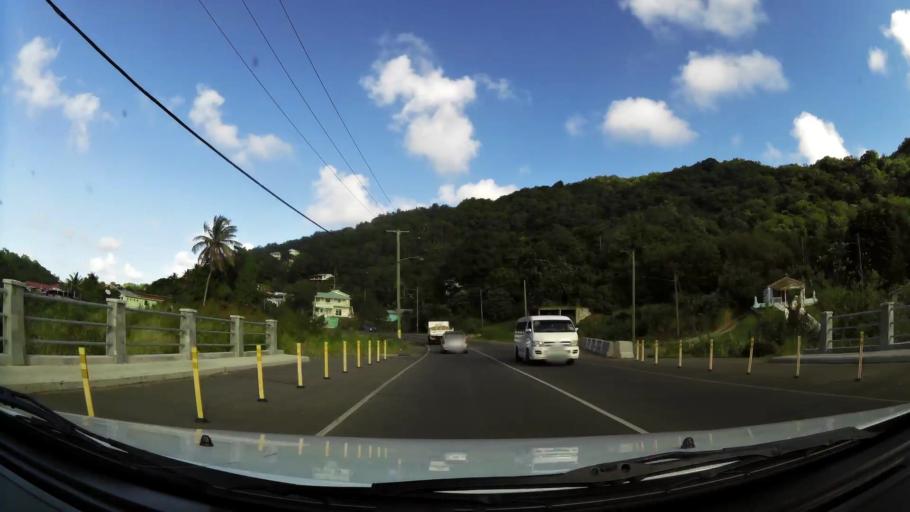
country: LC
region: Gros-Islet
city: Gros Islet
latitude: 14.0551
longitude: -60.9603
